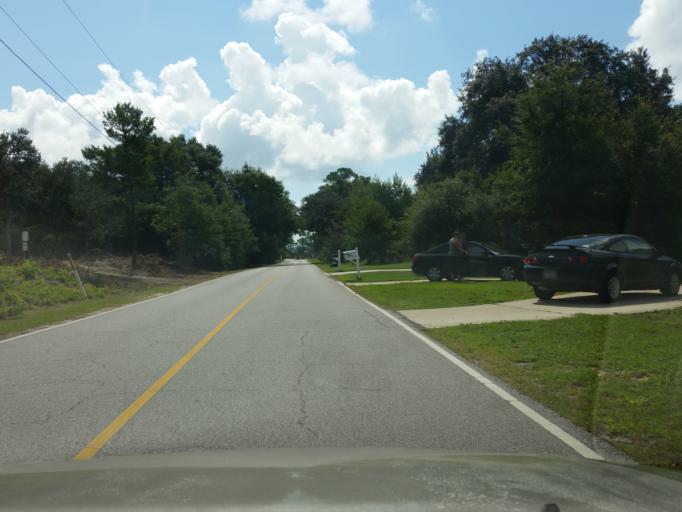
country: US
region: Alabama
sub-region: Baldwin County
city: Orange Beach
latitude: 30.3157
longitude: -87.4805
